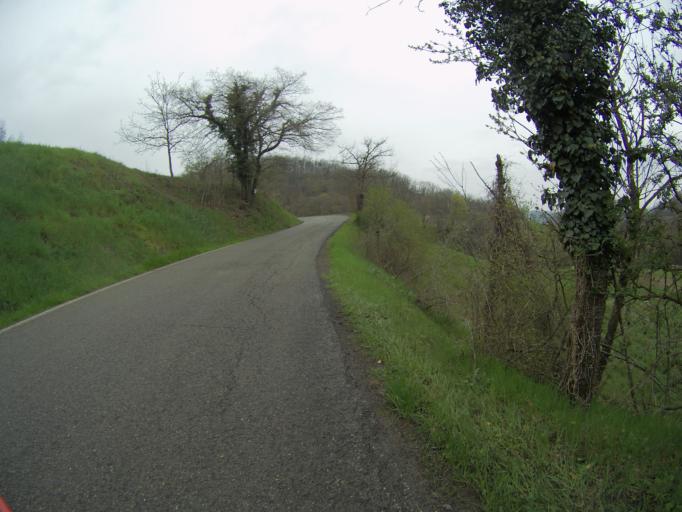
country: IT
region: Emilia-Romagna
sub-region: Provincia di Reggio Emilia
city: Casina
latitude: 44.5407
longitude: 10.4625
